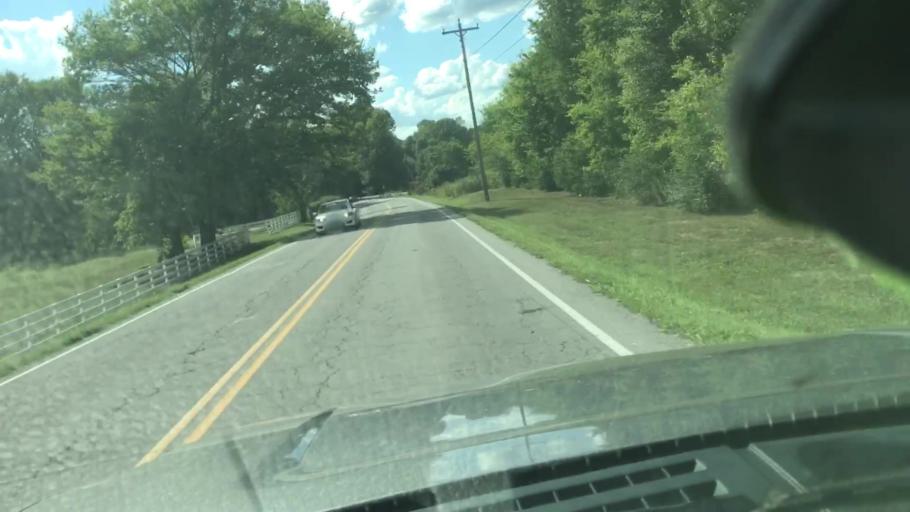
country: US
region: Tennessee
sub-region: Davidson County
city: Forest Hills
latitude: 36.0291
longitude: -86.9196
